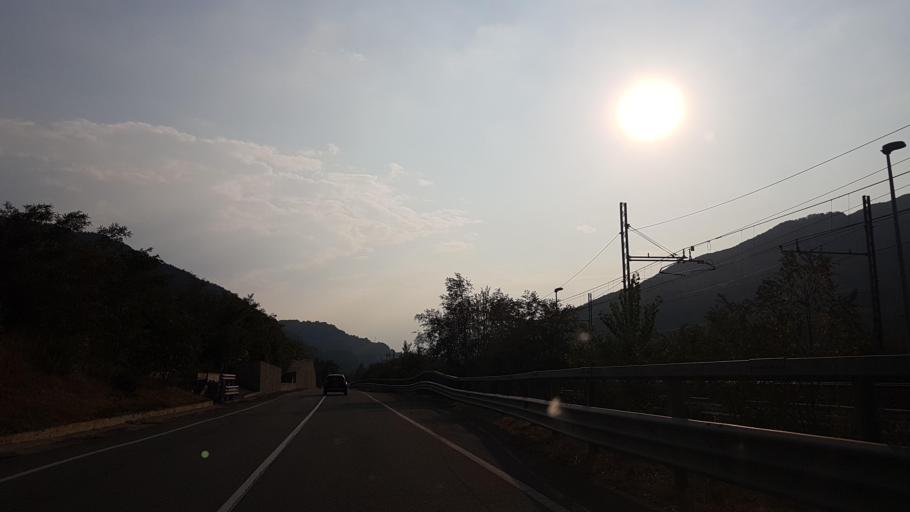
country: IT
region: Emilia-Romagna
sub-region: Provincia di Parma
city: Varano De' Melegari
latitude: 44.6393
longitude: 10.0400
